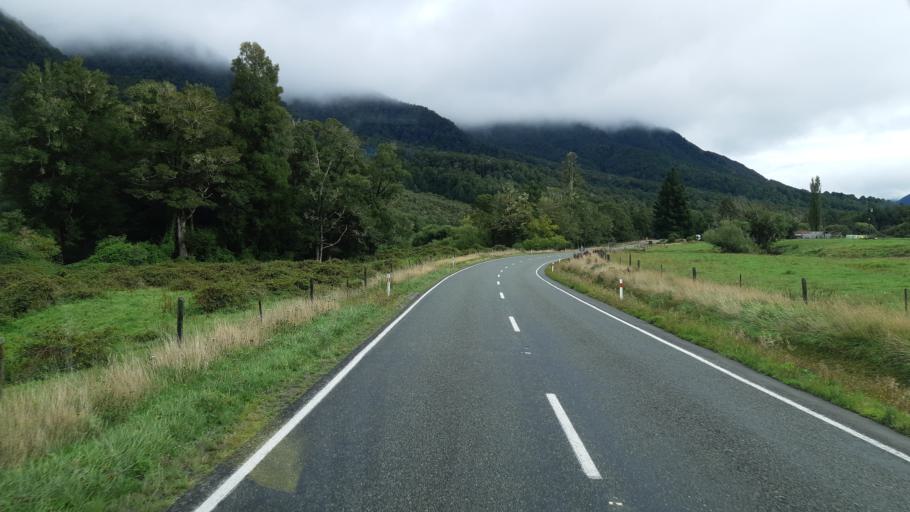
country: NZ
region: West Coast
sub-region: Buller District
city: Westport
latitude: -41.8872
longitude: 172.2477
